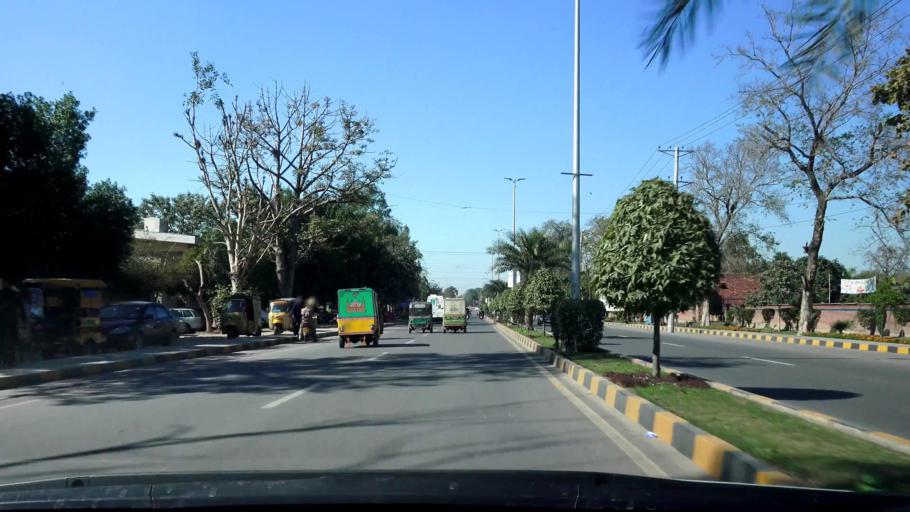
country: PK
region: Punjab
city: Faisalabad
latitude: 31.4242
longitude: 73.0812
